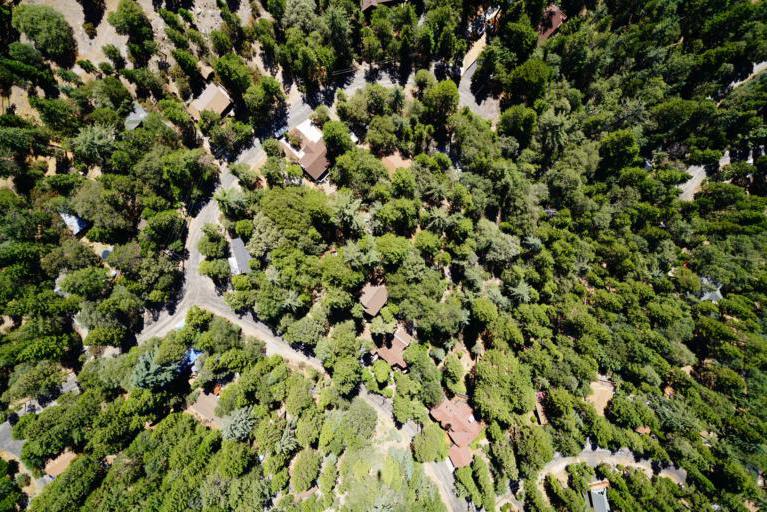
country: US
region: California
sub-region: Riverside County
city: Idyllwild-Pine Cove
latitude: 33.7526
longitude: -116.7479
